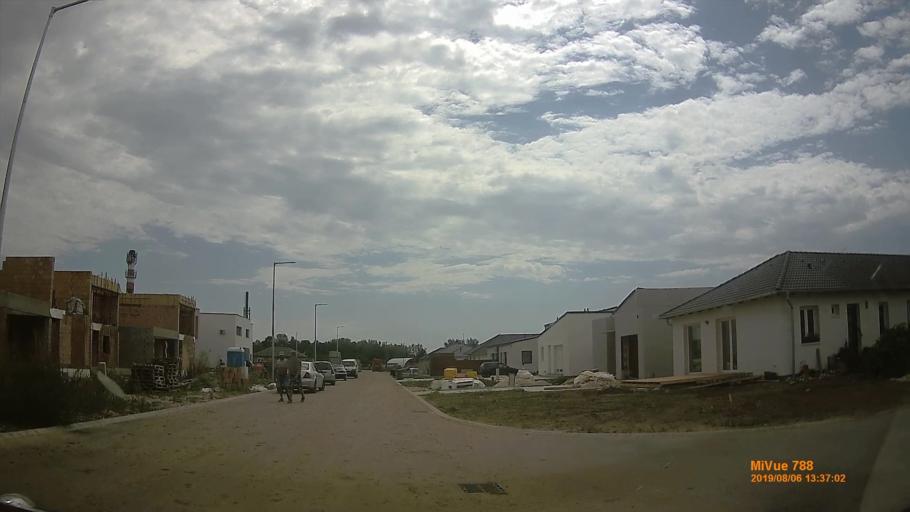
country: HU
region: Vas
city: Szombathely
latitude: 47.2499
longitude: 16.6016
